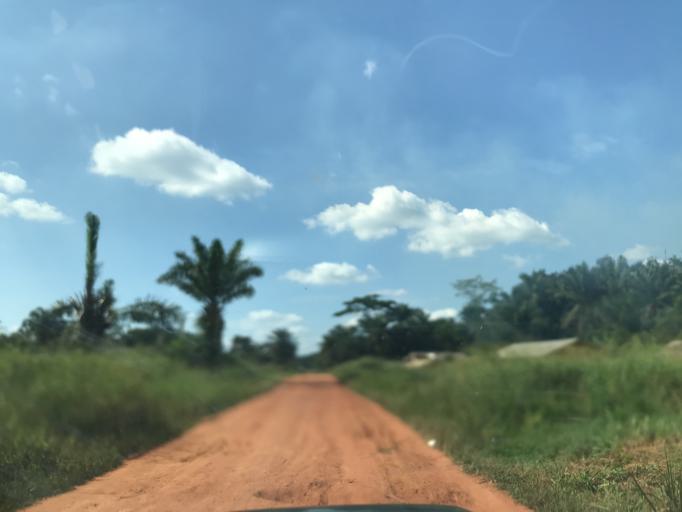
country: CD
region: Eastern Province
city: Kisangani
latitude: 1.1974
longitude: 25.2568
